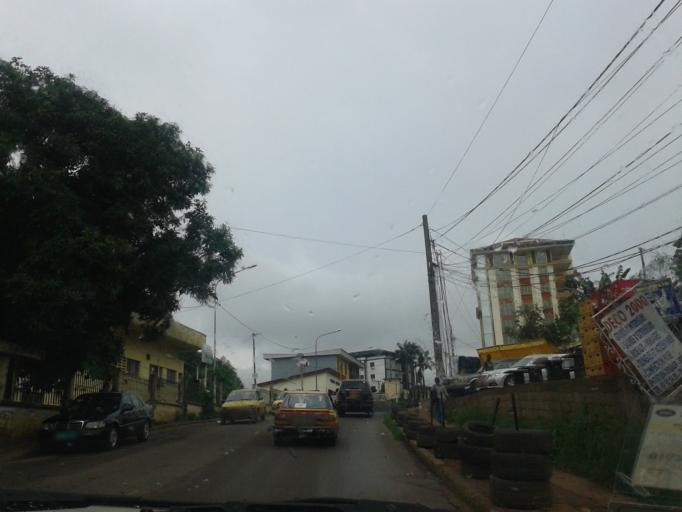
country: CM
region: Centre
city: Yaounde
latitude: 3.8856
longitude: 11.5176
